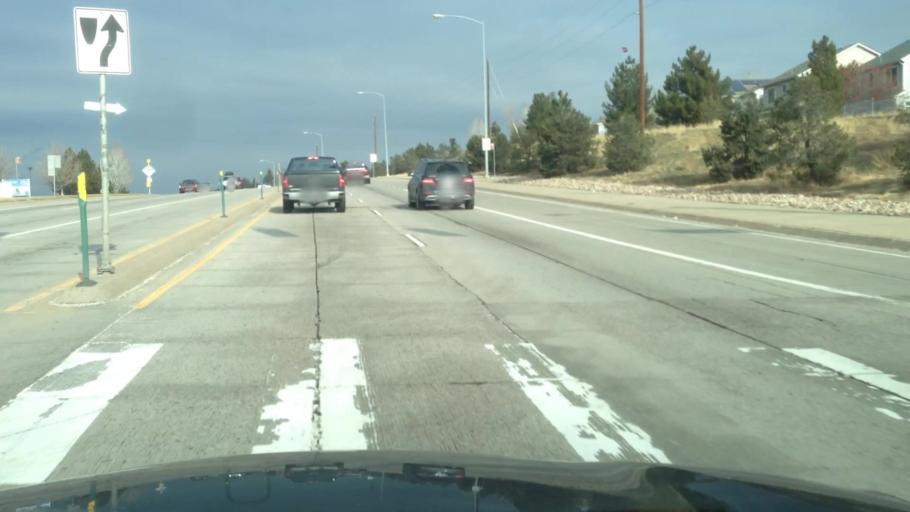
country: US
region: Colorado
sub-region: Arapahoe County
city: Dove Valley
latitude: 39.6240
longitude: -104.8216
